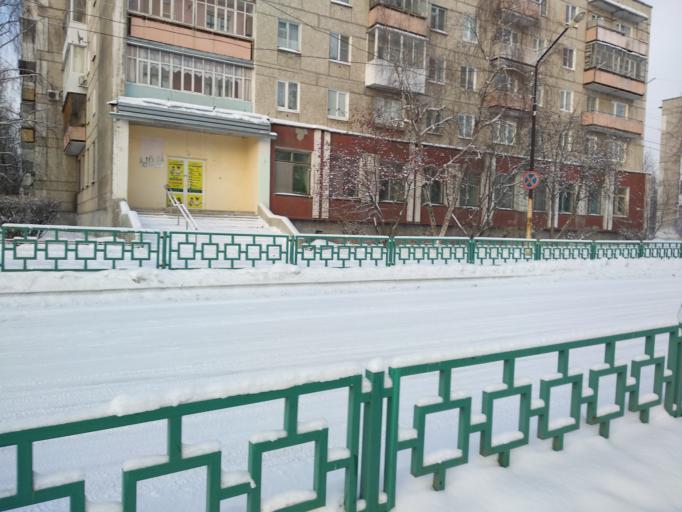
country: RU
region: Sverdlovsk
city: Krasnotur'insk
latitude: 59.7657
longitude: 60.2143
